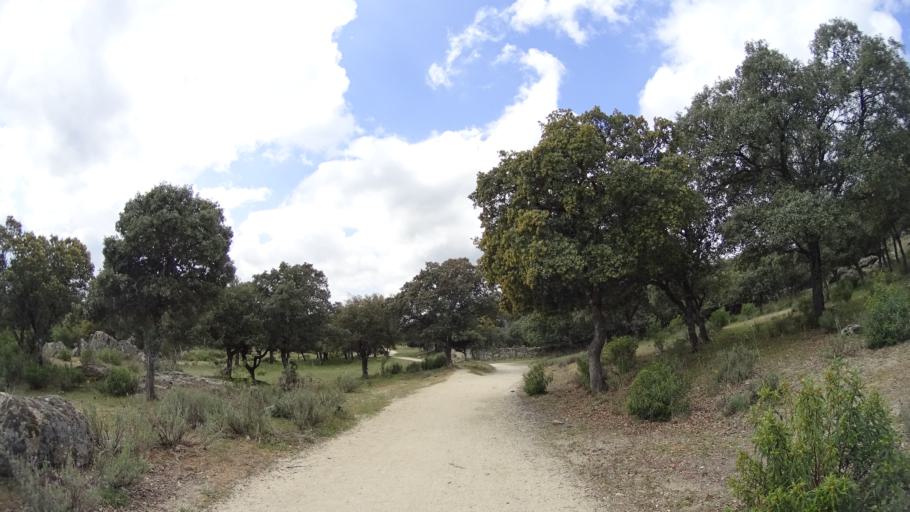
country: ES
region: Madrid
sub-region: Provincia de Madrid
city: Hoyo de Manzanares
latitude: 40.6225
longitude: -3.8847
